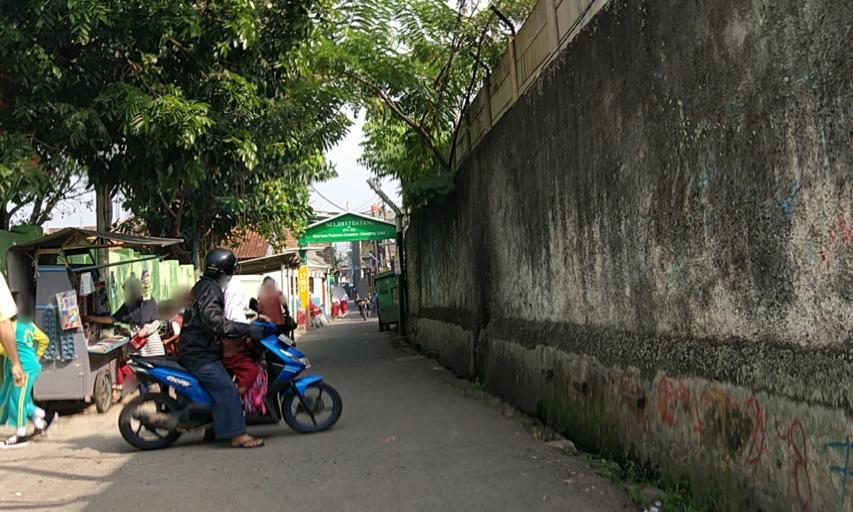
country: ID
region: West Java
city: Bandung
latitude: -6.9030
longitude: 107.6482
